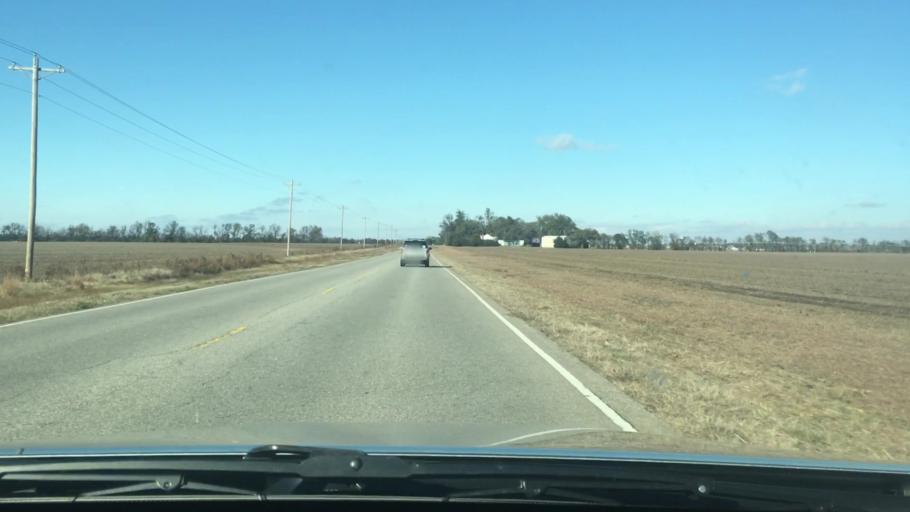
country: US
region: Kansas
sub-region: Sedgwick County
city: Maize
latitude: 37.7462
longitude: -97.4809
